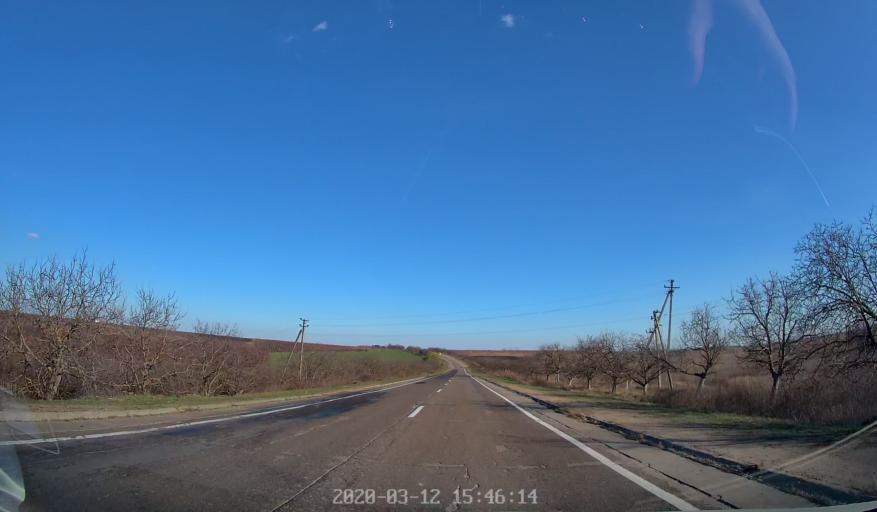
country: MD
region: Chisinau
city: Stauceni
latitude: 47.1008
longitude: 28.8891
